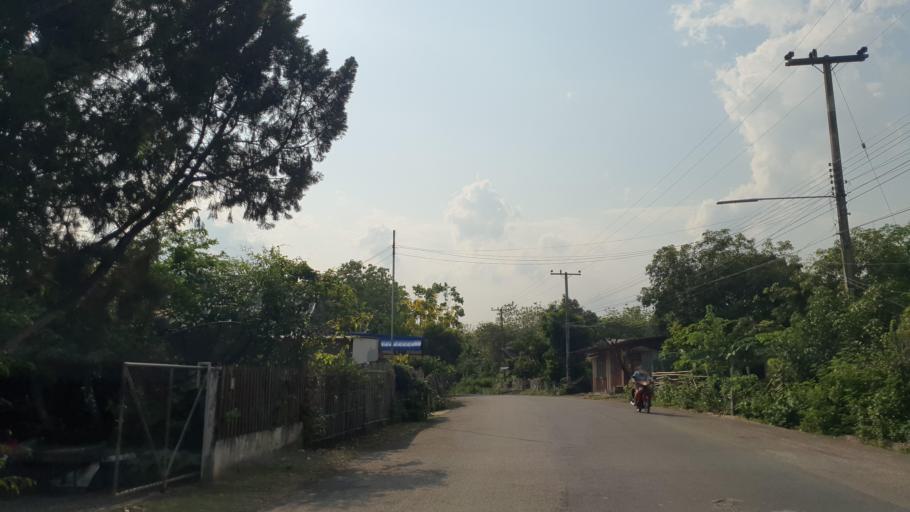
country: TH
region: Chiang Mai
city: Mae Wang
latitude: 18.6800
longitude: 98.8186
